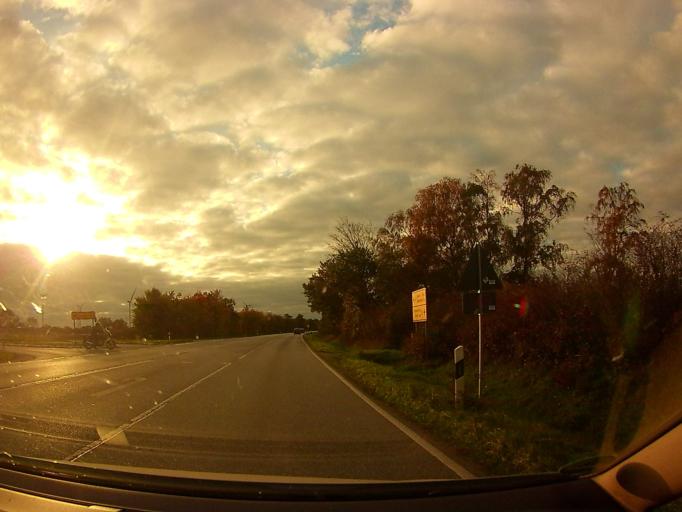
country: DE
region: Schleswig-Holstein
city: Ellingstedt
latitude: 54.5153
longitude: 9.4255
